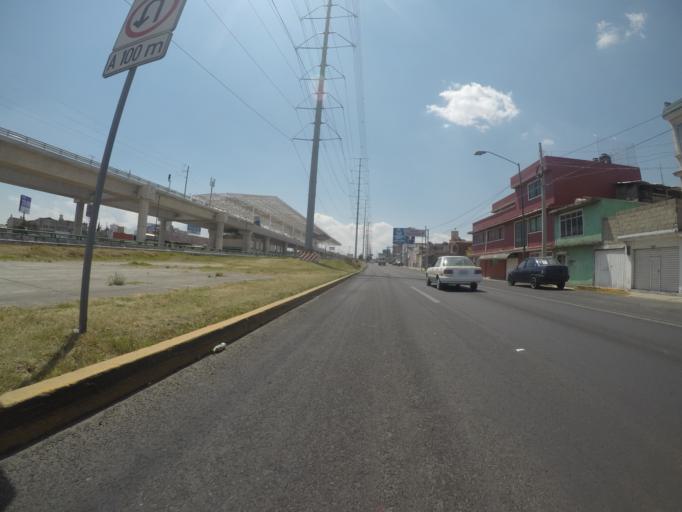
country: MX
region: Mexico
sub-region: Metepec
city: San Jorge Pueblo Nuevo
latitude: 19.2713
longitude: -99.6396
